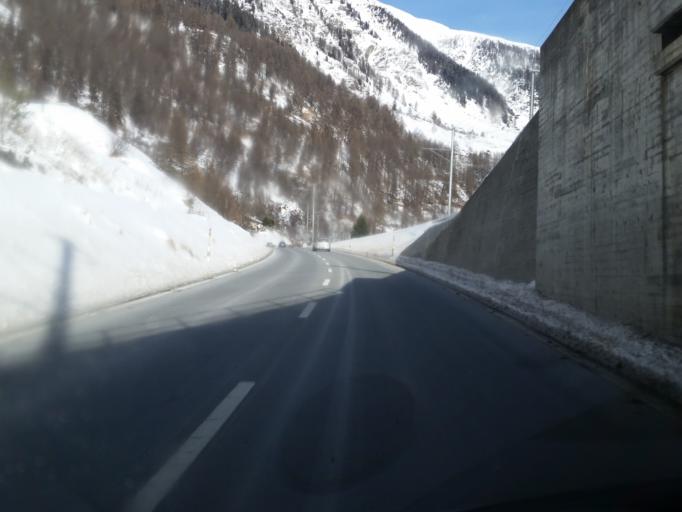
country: CH
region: Grisons
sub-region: Inn District
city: Zernez
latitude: 46.7665
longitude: 10.1083
